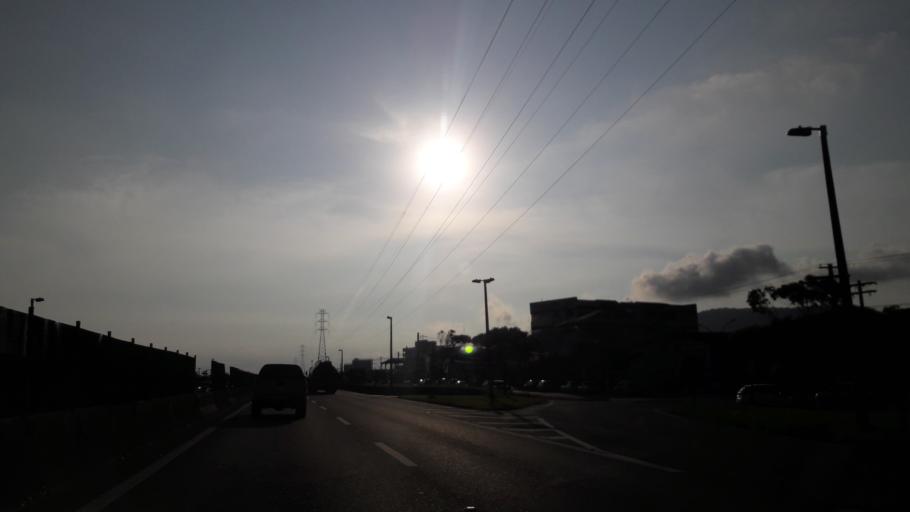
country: BR
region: Sao Paulo
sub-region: Mongagua
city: Mongagua
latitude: -24.1361
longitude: -46.7048
